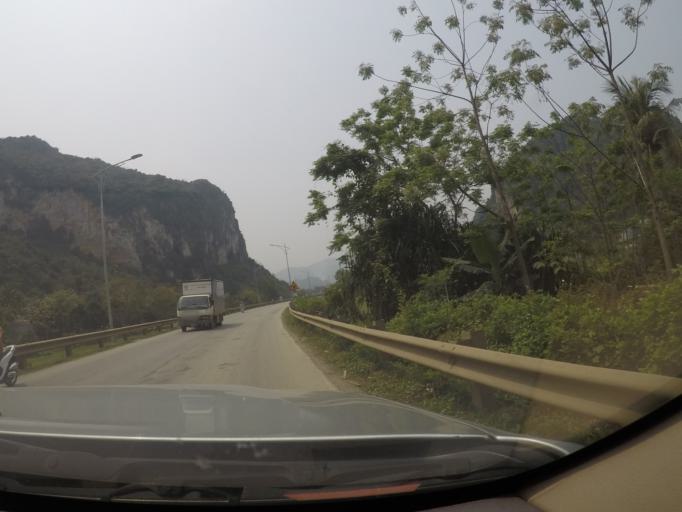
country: VN
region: Thanh Hoa
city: Thi Tran Cam Thuy
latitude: 20.2192
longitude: 105.4906
